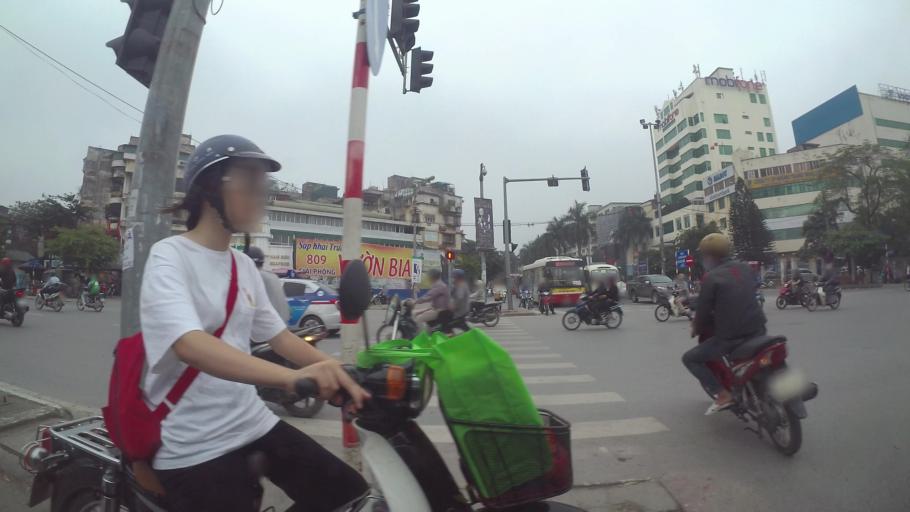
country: VN
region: Ha Noi
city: Hai BaTrung
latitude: 20.9839
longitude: 105.8410
